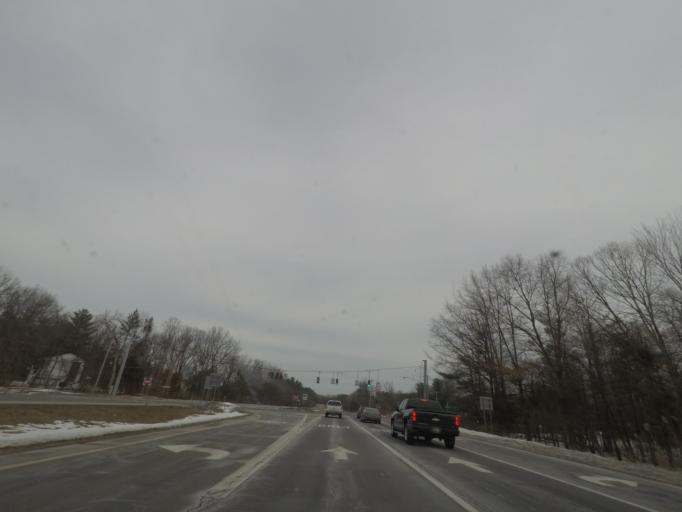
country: US
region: New York
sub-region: Albany County
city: Delmar
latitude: 42.6054
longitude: -73.8352
